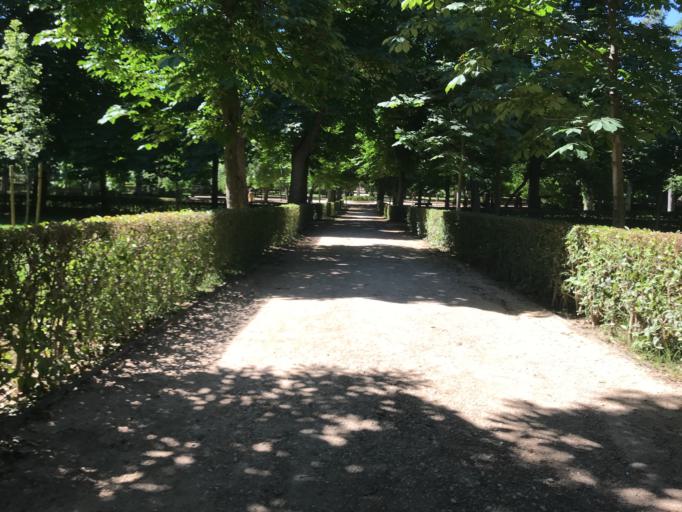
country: ES
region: Madrid
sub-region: Provincia de Madrid
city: Retiro
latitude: 40.4181
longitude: -3.6879
